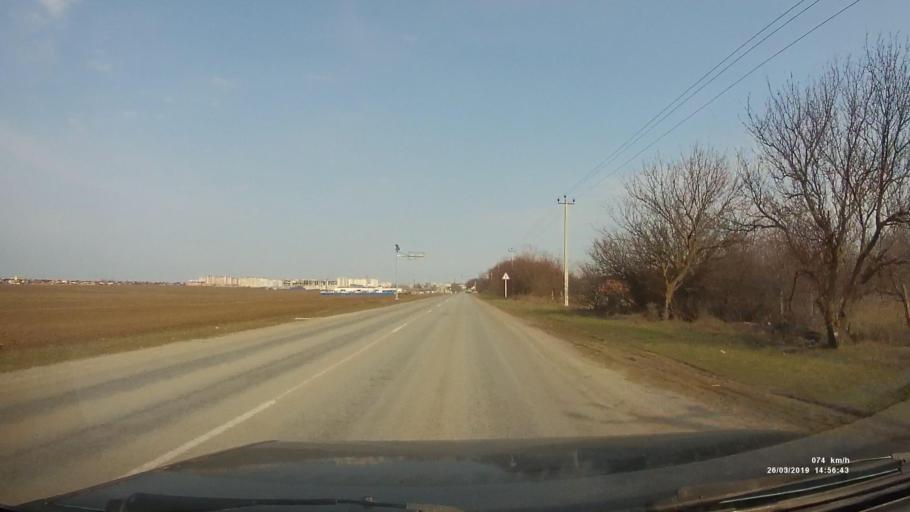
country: RU
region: Rostov
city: Novobessergenovka
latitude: 47.2069
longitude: 38.8328
